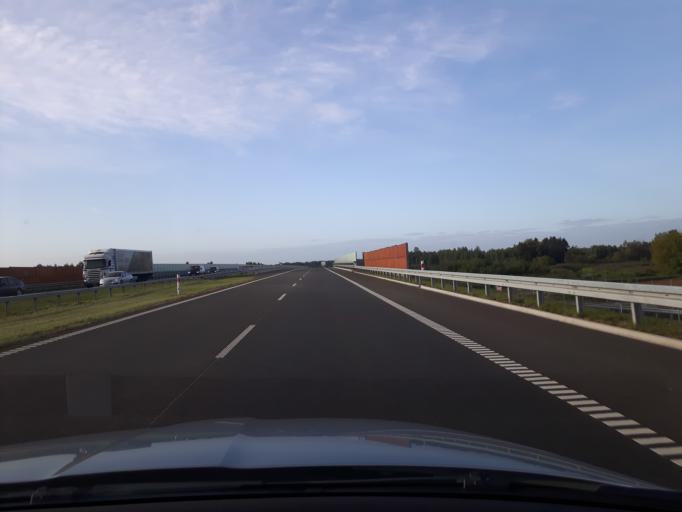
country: PL
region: Masovian Voivodeship
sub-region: Powiat radomski
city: Jedlinsk
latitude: 51.4995
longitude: 21.0779
